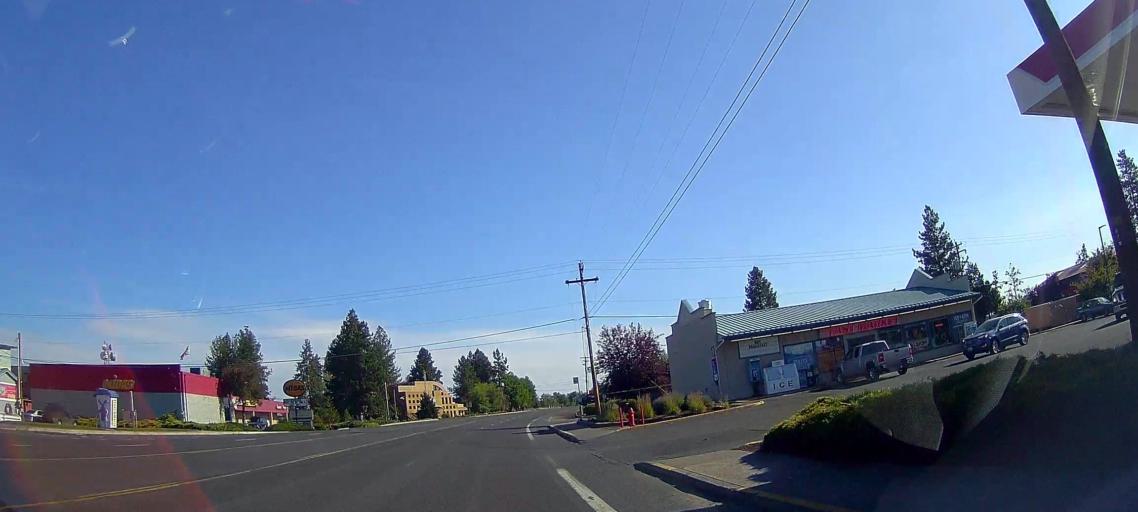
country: US
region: Oregon
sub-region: Deschutes County
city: Bend
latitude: 44.0868
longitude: -121.3061
